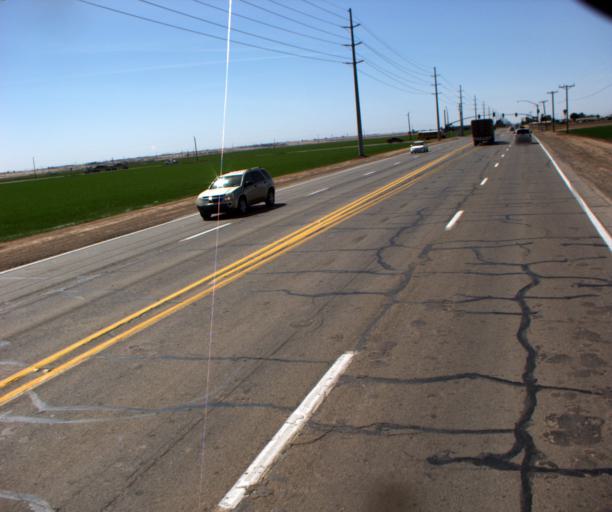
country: US
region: Arizona
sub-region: Yuma County
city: Yuma
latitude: 32.6993
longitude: -114.5192
